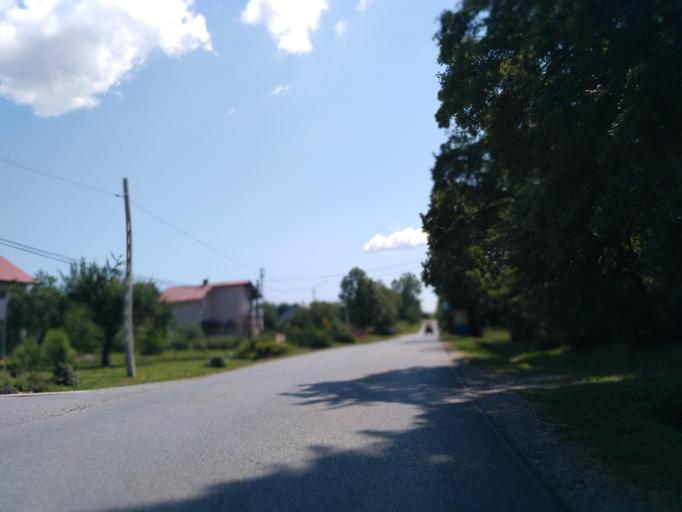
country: PL
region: Subcarpathian Voivodeship
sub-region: Powiat sanocki
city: Niebieszczany
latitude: 49.5099
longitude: 22.1501
